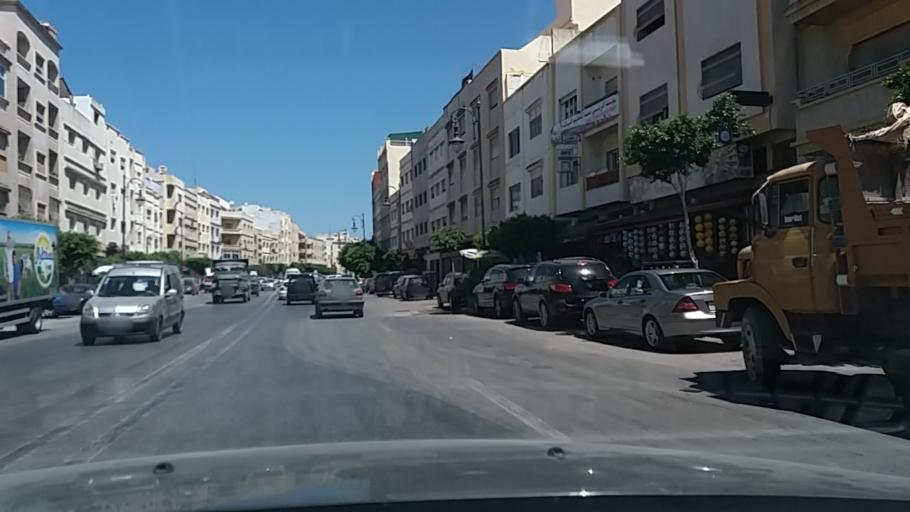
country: MA
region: Tanger-Tetouan
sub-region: Tanger-Assilah
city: Tangier
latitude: 35.7592
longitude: -5.7960
